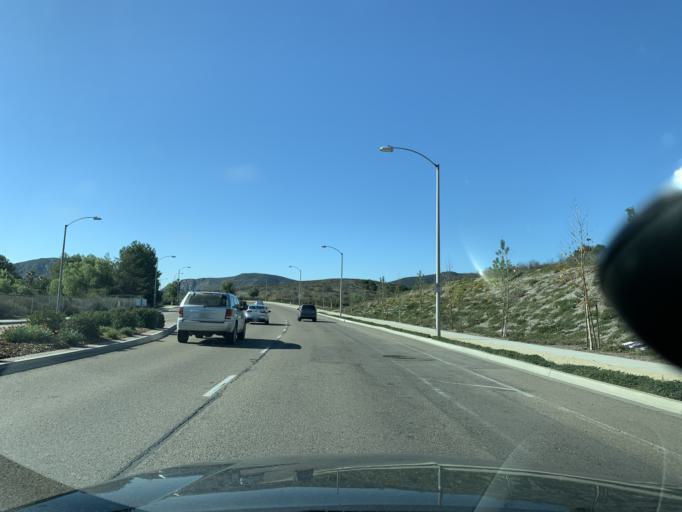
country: US
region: California
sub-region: San Diego County
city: Santee
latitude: 32.8488
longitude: -117.0192
